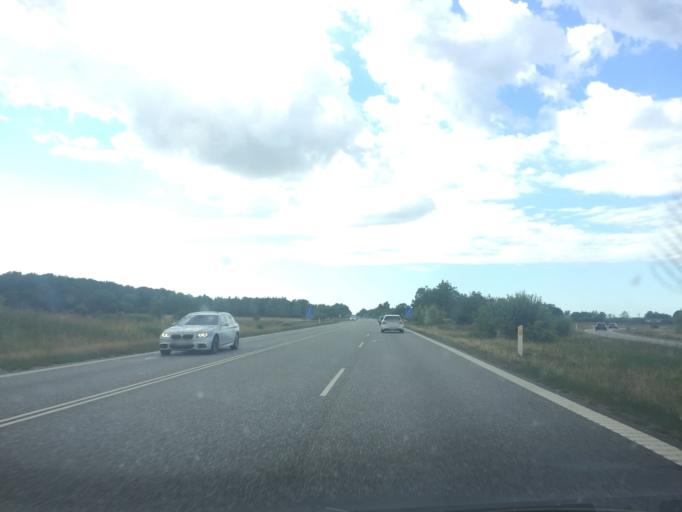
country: DK
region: Capital Region
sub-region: Hillerod Kommune
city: Hillerod
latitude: 55.9179
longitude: 12.2623
